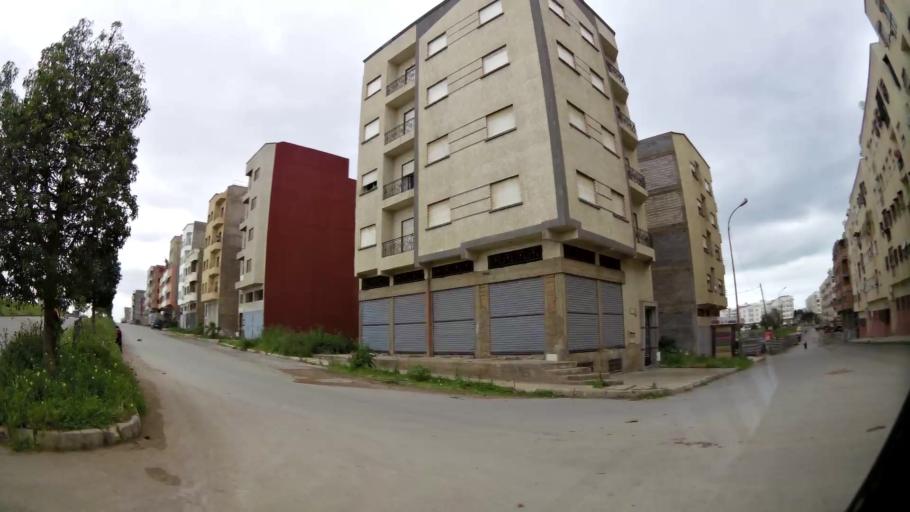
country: MA
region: Grand Casablanca
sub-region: Mediouna
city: Tit Mellil
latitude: 33.5564
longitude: -7.5314
